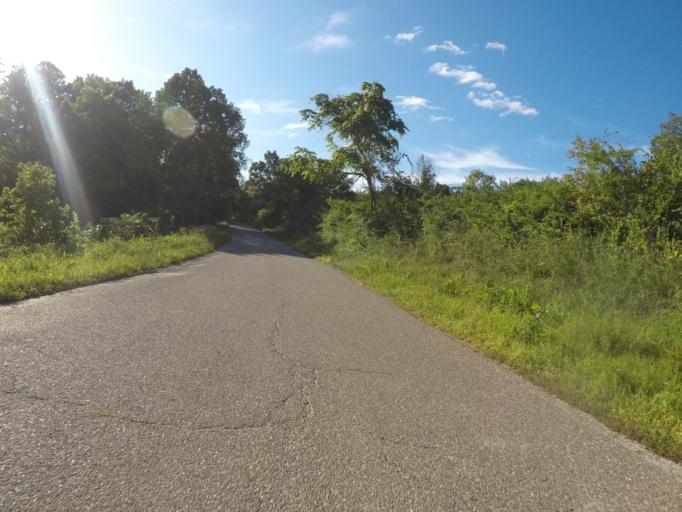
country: US
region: West Virginia
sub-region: Cabell County
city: Huntington
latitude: 38.4733
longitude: -82.4586
